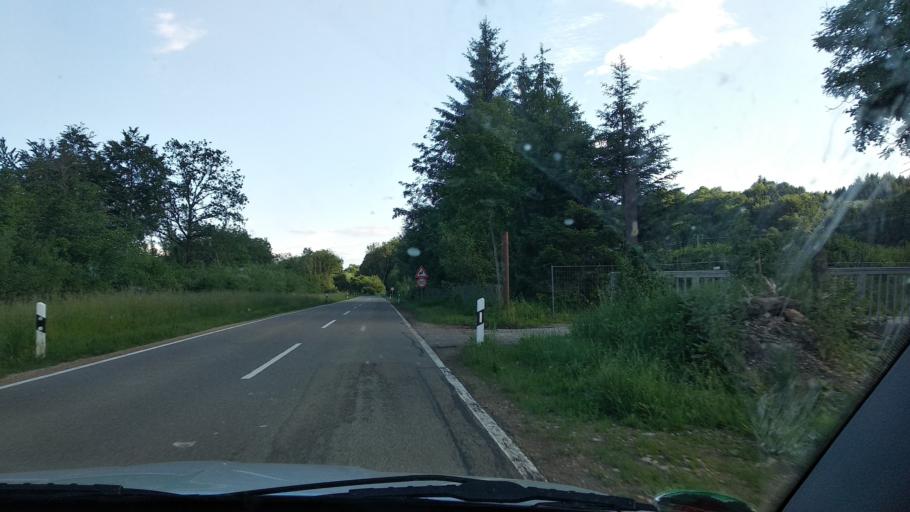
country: DE
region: Baden-Wuerttemberg
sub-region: Tuebingen Region
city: Aitrach
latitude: 47.9524
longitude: 10.0817
